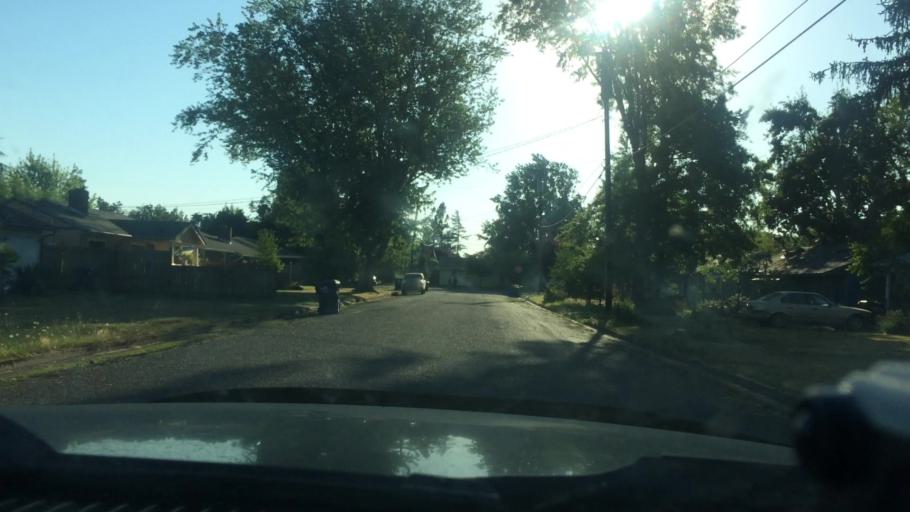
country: US
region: Oregon
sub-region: Lane County
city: Eugene
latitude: 44.0412
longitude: -123.1112
